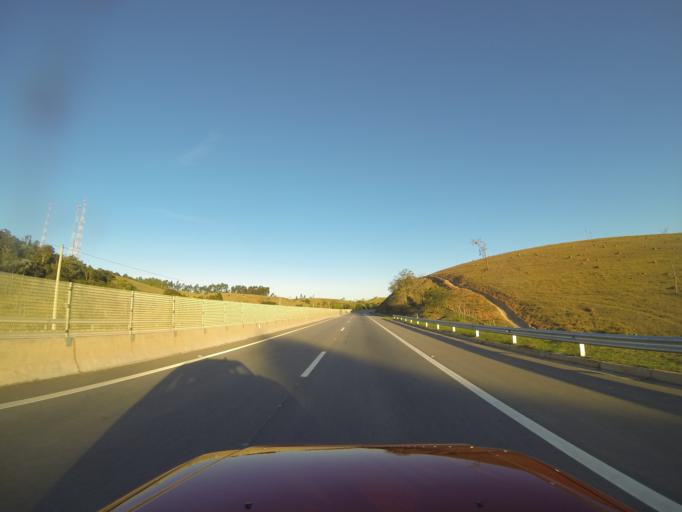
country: BR
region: Sao Paulo
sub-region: Santa Branca
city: Santa Branca
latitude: -23.4333
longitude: -45.6229
